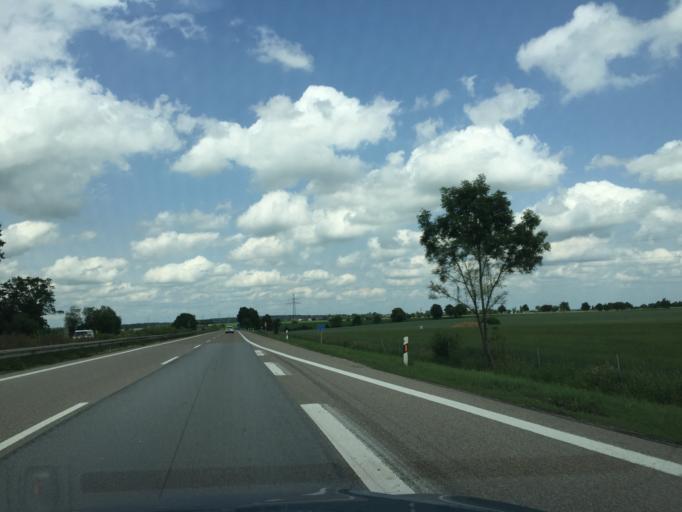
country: DE
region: Bavaria
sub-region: Swabia
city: Senden
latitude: 48.3298
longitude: 10.0887
